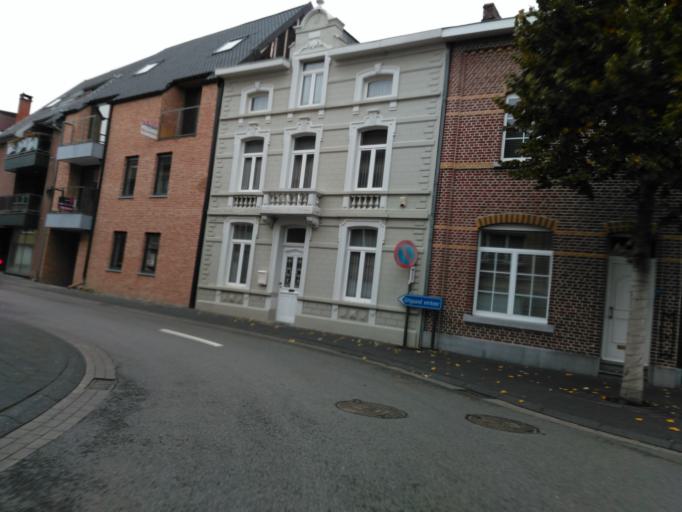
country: BE
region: Flanders
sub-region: Provincie Limburg
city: Bilzen
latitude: 50.8719
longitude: 5.5164
